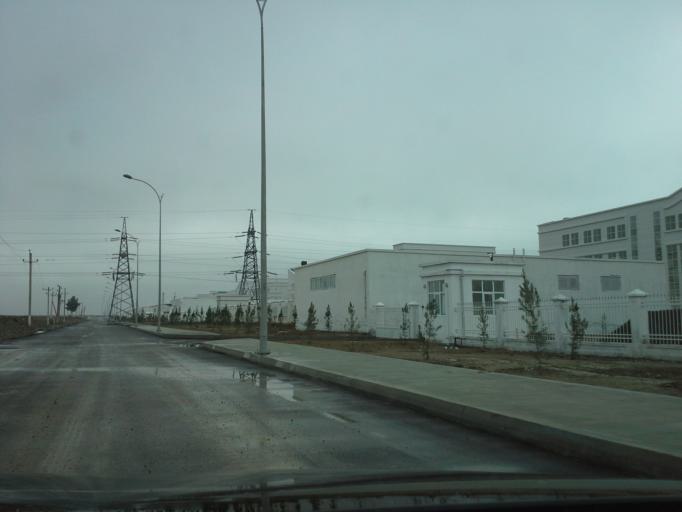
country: TM
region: Ahal
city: Ashgabat
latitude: 37.9589
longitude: 58.4239
